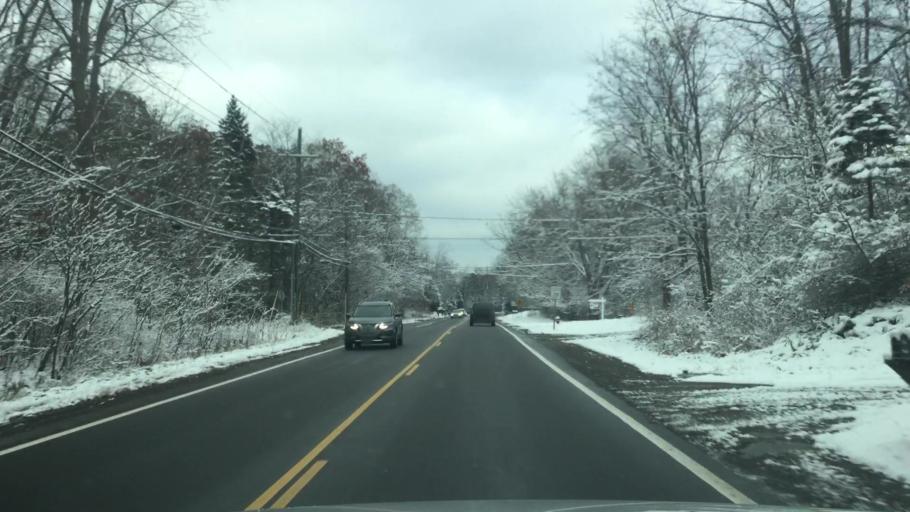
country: US
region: Michigan
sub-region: Oakland County
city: West Bloomfield Township
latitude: 42.5699
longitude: -83.4031
